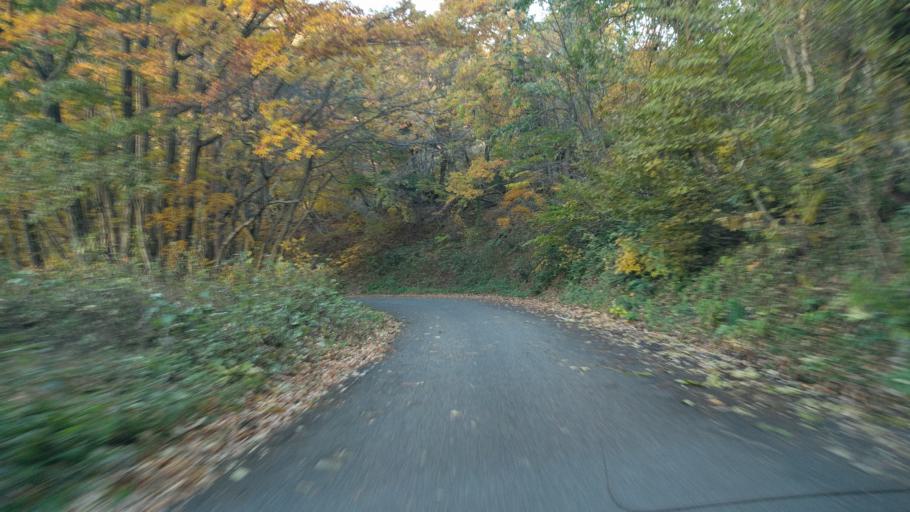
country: JP
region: Fukushima
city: Kitakata
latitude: 37.4583
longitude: 139.6166
